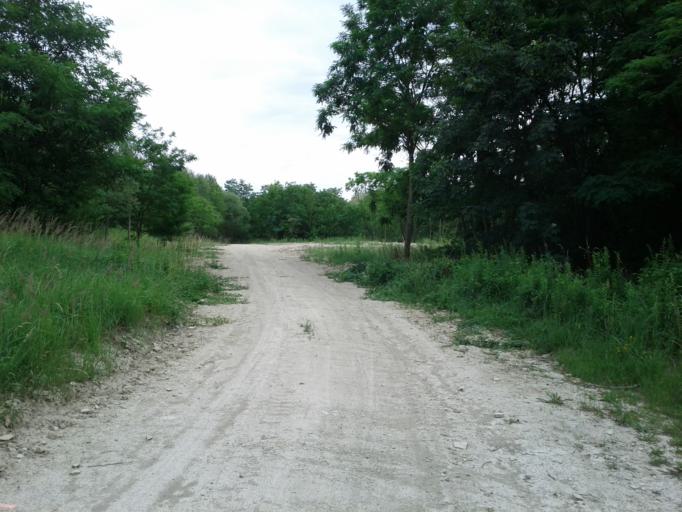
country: DE
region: Brandenburg
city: Woltersdorf
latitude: 52.4759
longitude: 13.8040
